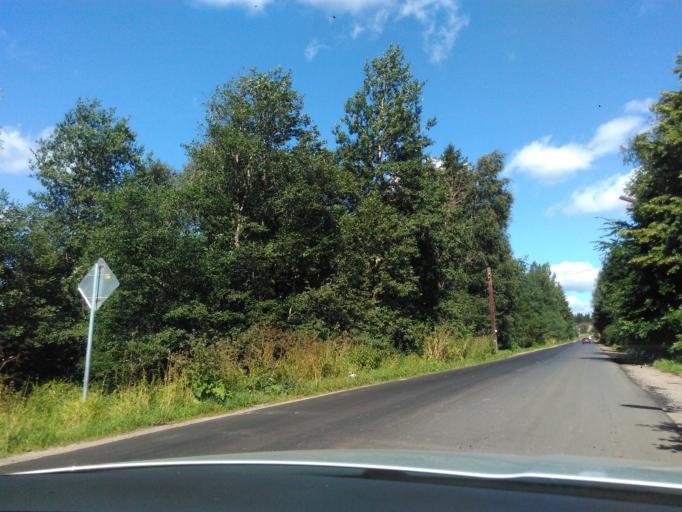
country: RU
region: Moskovskaya
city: Klin
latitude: 56.2370
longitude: 36.8355
